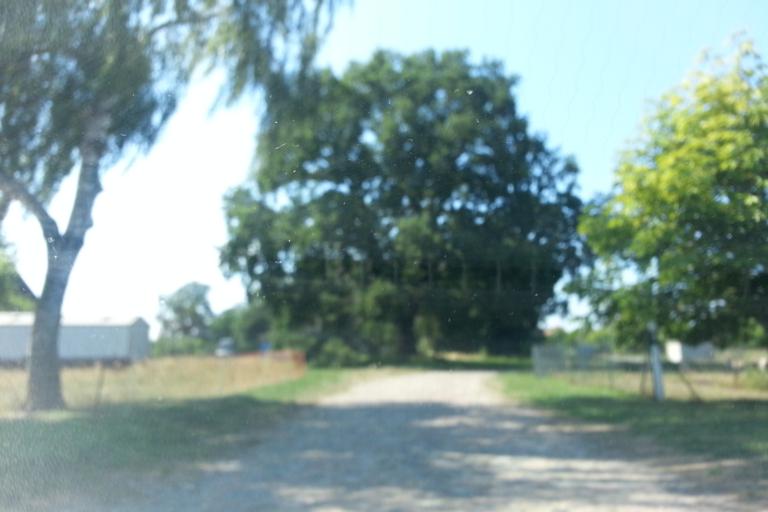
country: DE
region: Mecklenburg-Vorpommern
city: Ducherow
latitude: 53.6991
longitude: 13.8069
